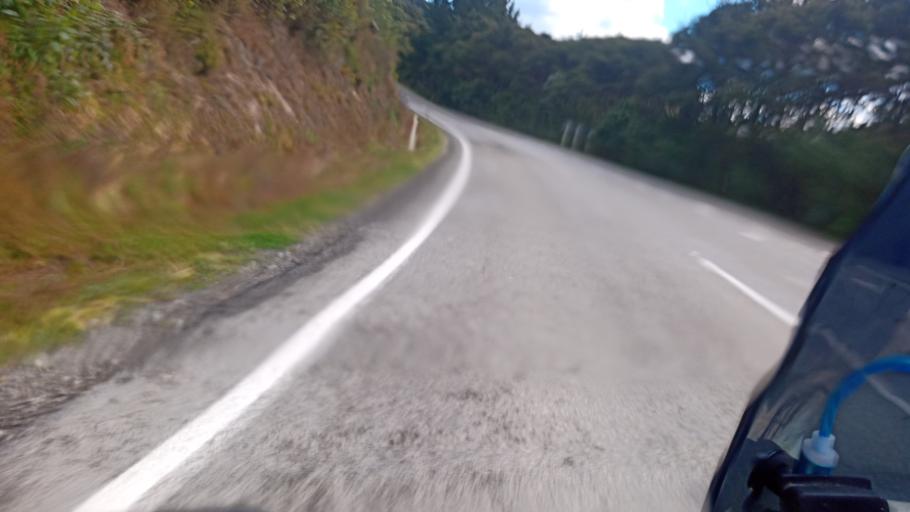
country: NZ
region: Gisborne
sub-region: Gisborne District
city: Gisborne
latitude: -37.9859
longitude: 178.2752
